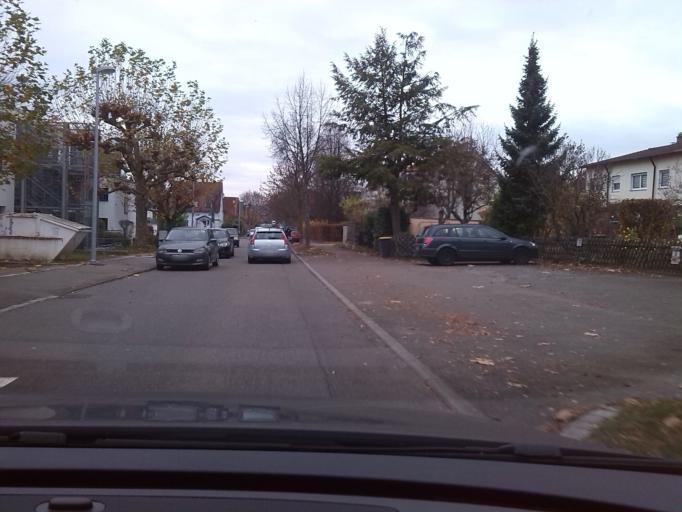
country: DE
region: Baden-Wuerttemberg
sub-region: Regierungsbezirk Stuttgart
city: Fellbach
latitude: 48.8164
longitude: 9.2470
